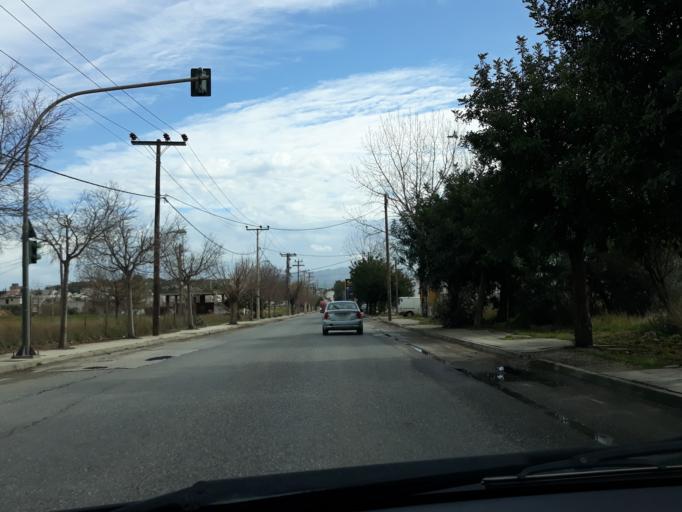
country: GR
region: Attica
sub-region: Nomarchia Dytikis Attikis
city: Ano Liosia
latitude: 38.0798
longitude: 23.7118
